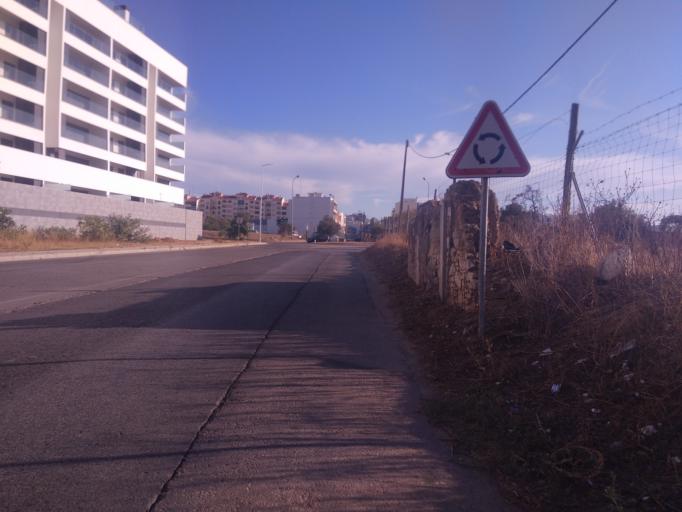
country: PT
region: Faro
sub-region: Faro
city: Faro
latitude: 37.0305
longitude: -7.9399
